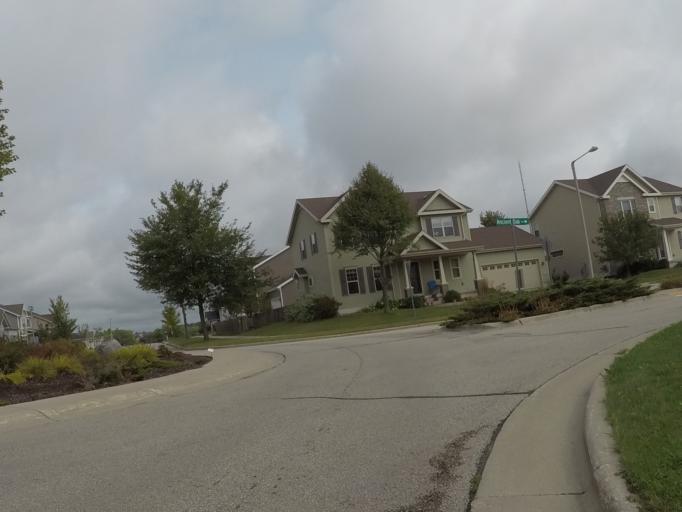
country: US
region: Wisconsin
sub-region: Dane County
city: Verona
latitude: 43.0437
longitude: -89.5468
